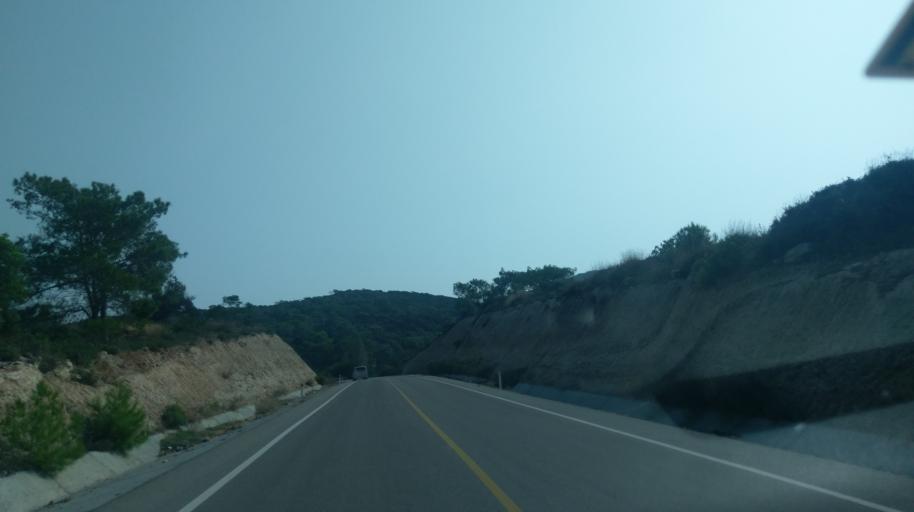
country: CY
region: Ammochostos
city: Leonarisso
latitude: 35.4550
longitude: 34.0047
